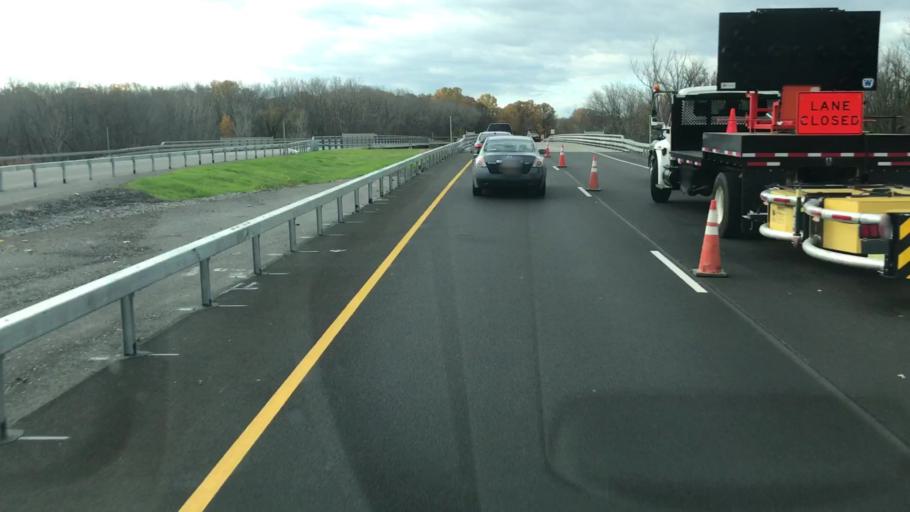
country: US
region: New York
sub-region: Onondaga County
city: Lakeland
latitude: 43.1220
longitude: -76.2491
